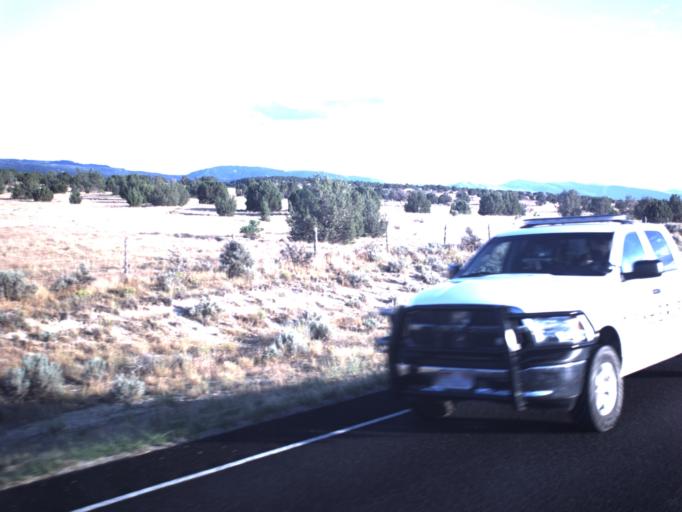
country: US
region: Utah
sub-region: Sanpete County
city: Moroni
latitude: 39.4640
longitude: -111.5350
